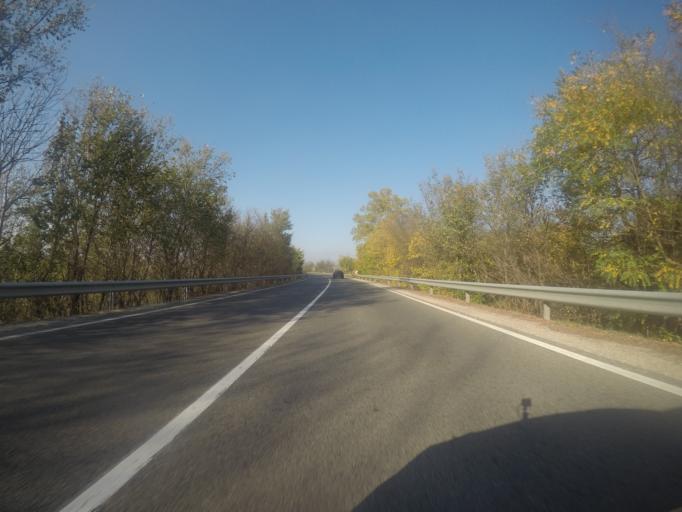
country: HU
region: Fejer
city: Ercsi
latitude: 47.2294
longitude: 18.8932
